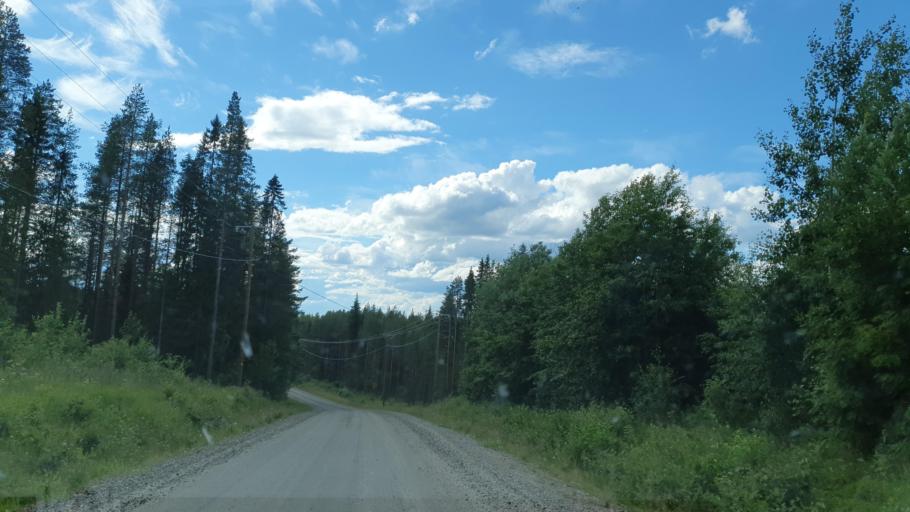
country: FI
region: Kainuu
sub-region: Kehys-Kainuu
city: Kuhmo
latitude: 64.1666
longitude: 29.8705
